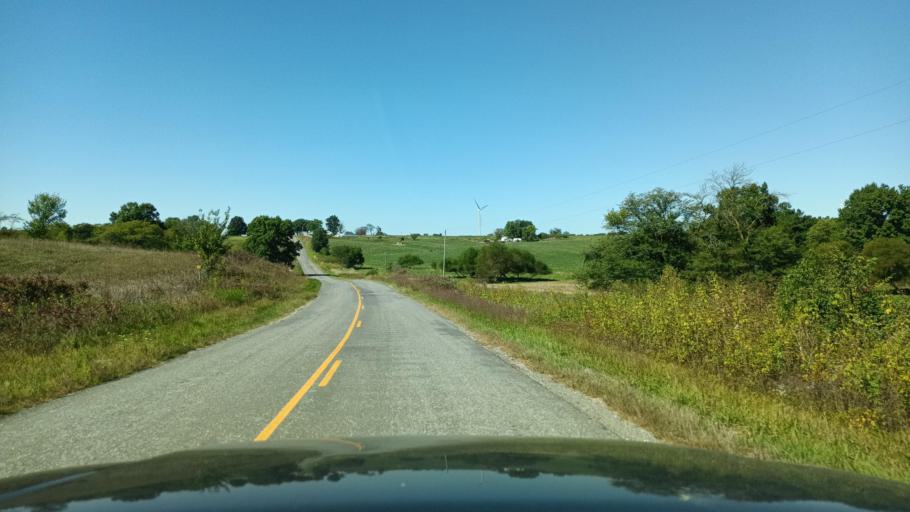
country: US
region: Missouri
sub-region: Adair County
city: Kirksville
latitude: 40.3307
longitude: -92.5077
